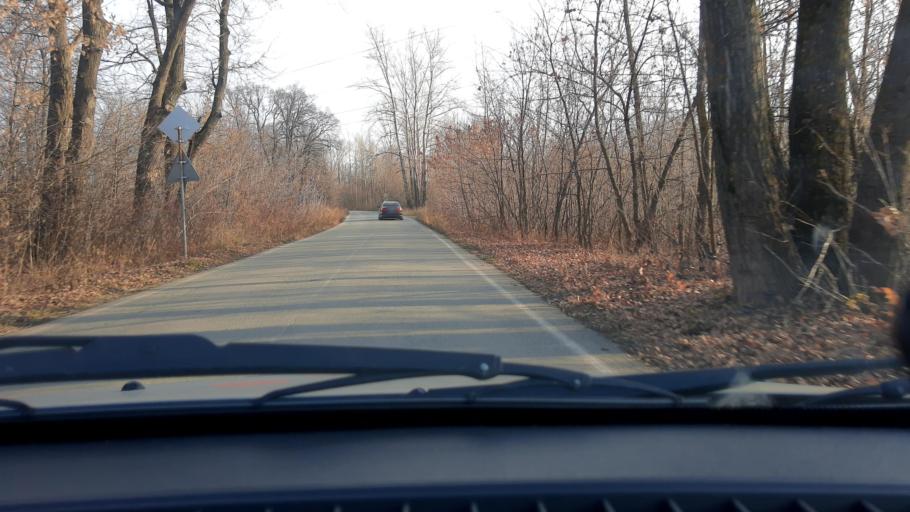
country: RU
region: Bashkortostan
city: Ufa
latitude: 54.6652
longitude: 55.9614
